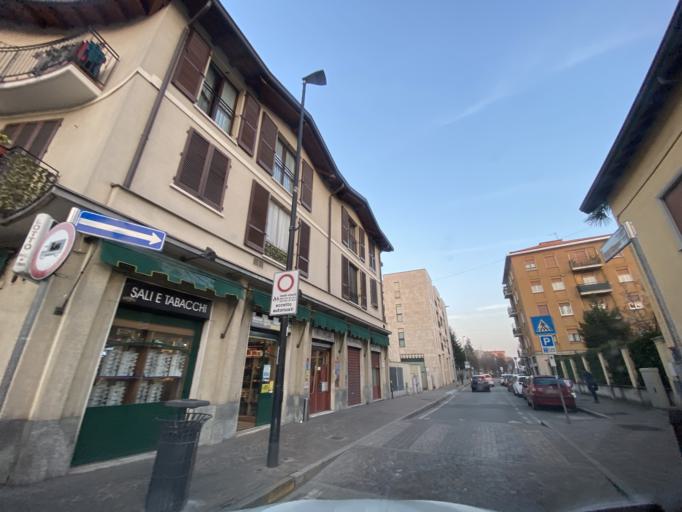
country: IT
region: Lombardy
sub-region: Provincia di Monza e Brianza
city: Limbiate
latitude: 45.6035
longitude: 9.1210
